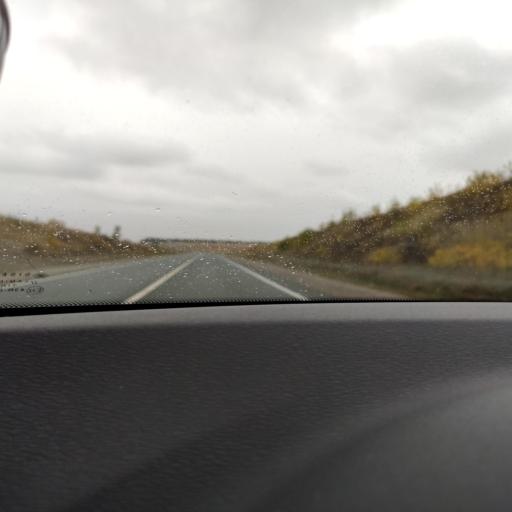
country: RU
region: Samara
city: Mirnyy
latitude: 53.5963
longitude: 50.2774
